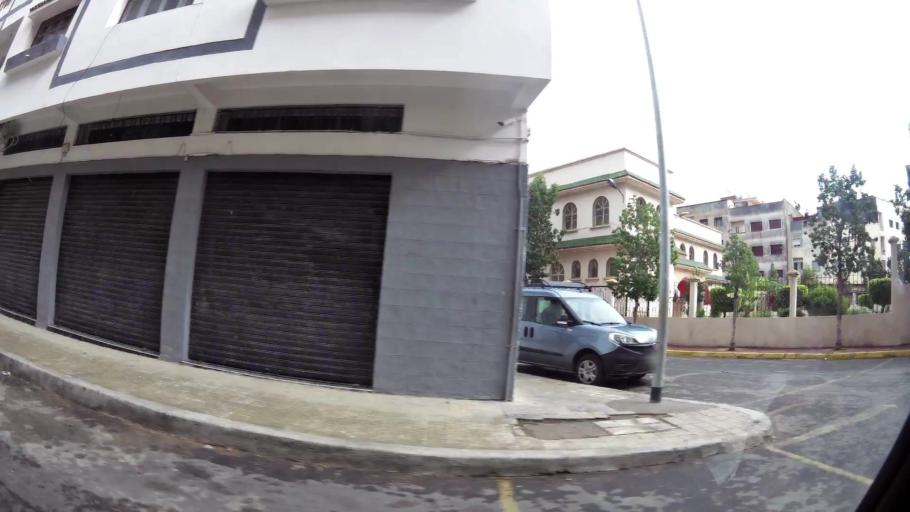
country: MA
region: Grand Casablanca
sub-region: Casablanca
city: Casablanca
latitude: 33.5651
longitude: -7.6736
